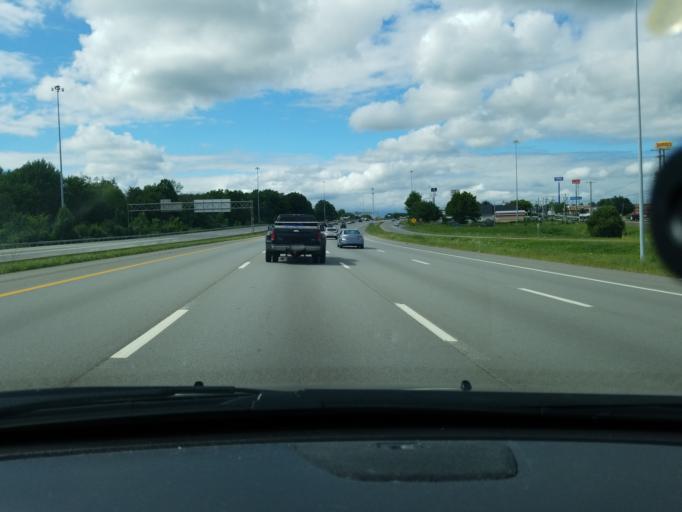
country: US
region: Ohio
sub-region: Summit County
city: Portage Lakes
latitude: 40.9888
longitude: -81.4930
